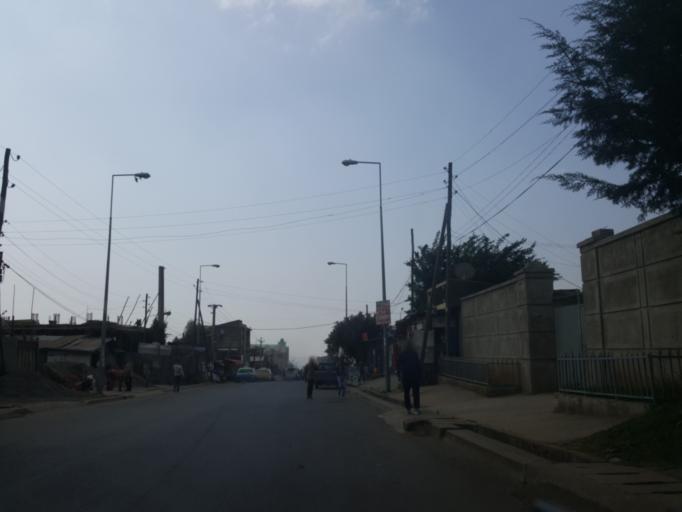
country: ET
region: Adis Abeba
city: Addis Ababa
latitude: 9.0664
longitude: 38.7212
